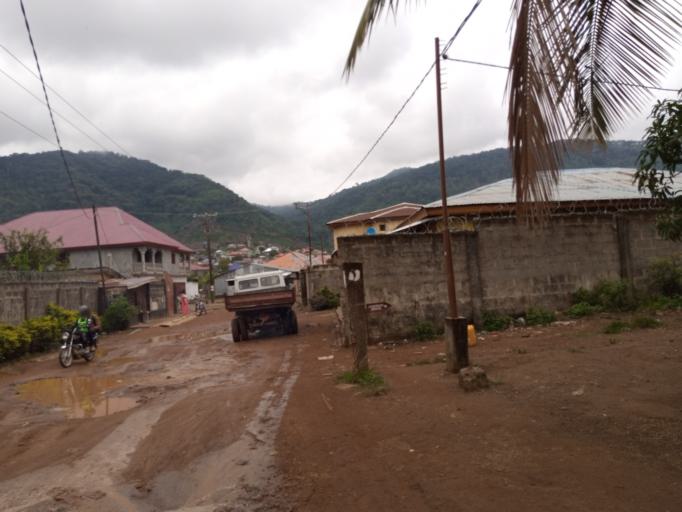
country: SL
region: Western Area
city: Hastings
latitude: 8.3806
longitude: -13.1511
